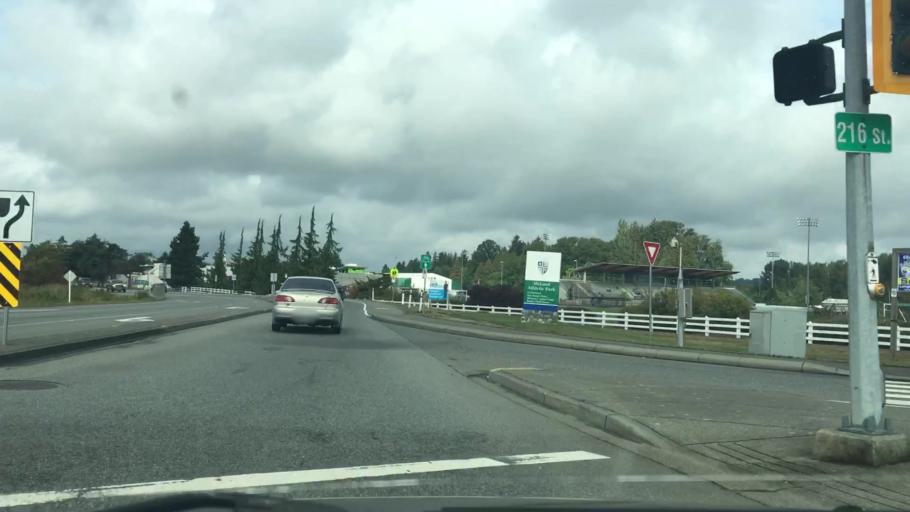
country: CA
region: British Columbia
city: Langley
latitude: 49.1041
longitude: -122.6246
